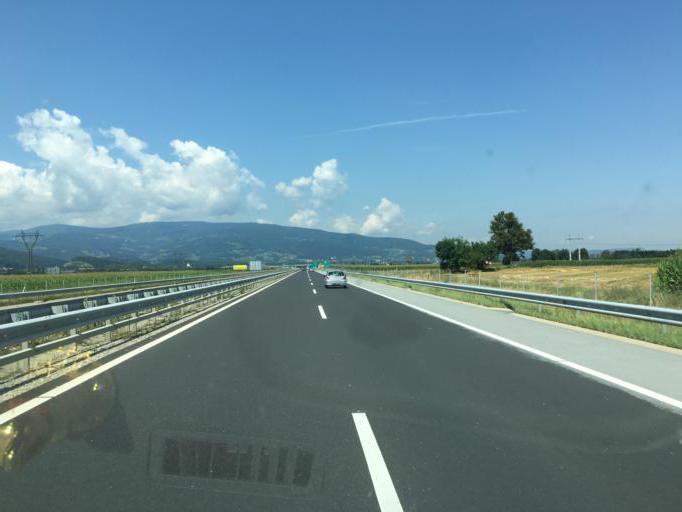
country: SI
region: Race-Fram
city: Race
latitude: 46.4695
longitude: 15.6859
